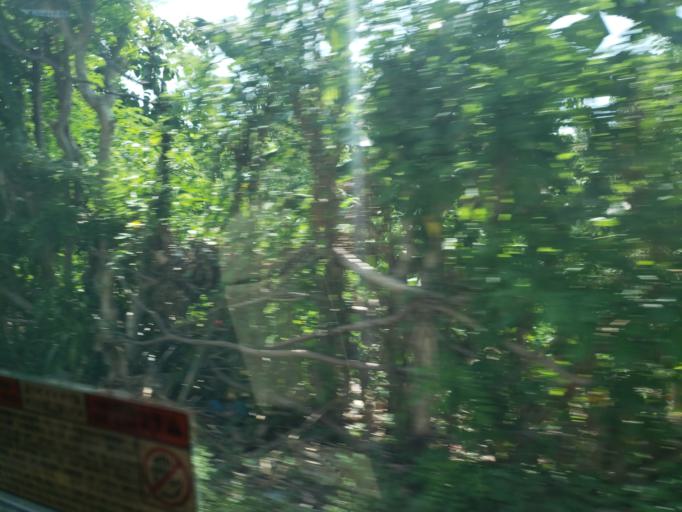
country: ID
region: Bali
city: Kangin
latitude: -8.8335
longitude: 115.1494
